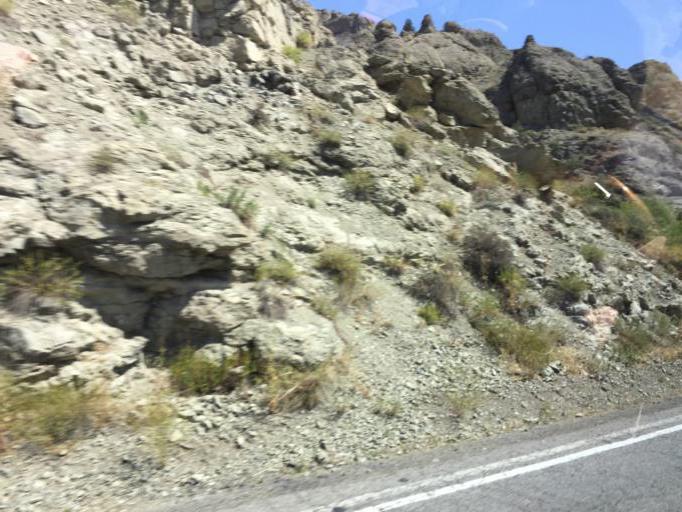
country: AM
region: Vayots' Dzori Marz
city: Zarrit'ap'
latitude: 39.7007
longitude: 45.5910
